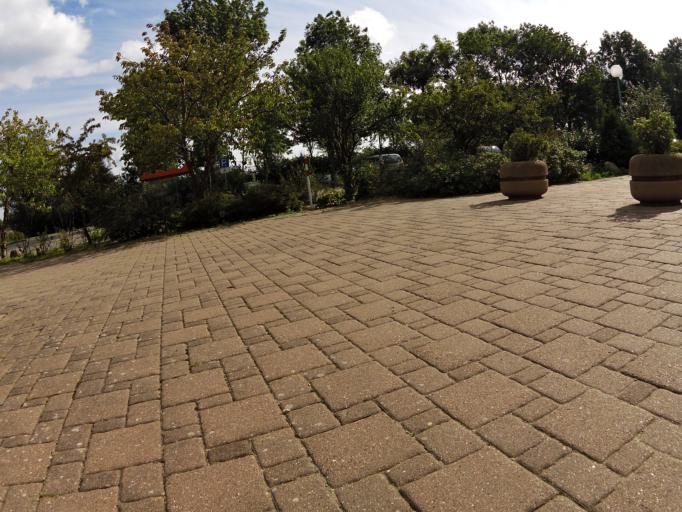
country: DE
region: Schleswig-Holstein
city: Wisch
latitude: 54.4232
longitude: 10.3701
